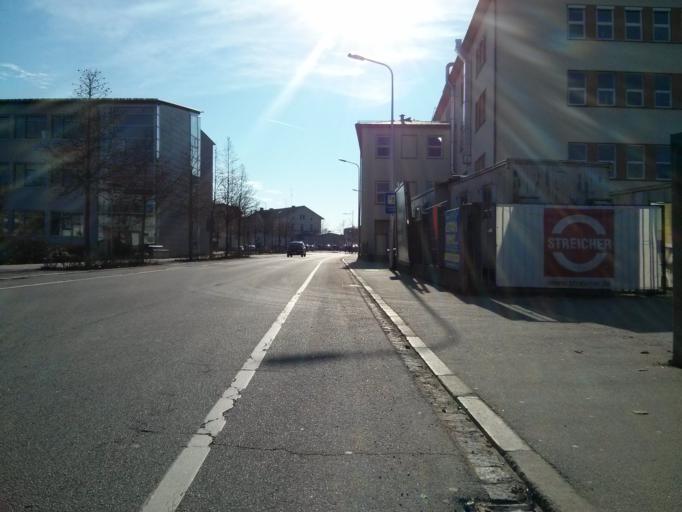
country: DE
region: Bavaria
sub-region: Lower Bavaria
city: Deggendorf
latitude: 48.8409
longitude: 12.9522
